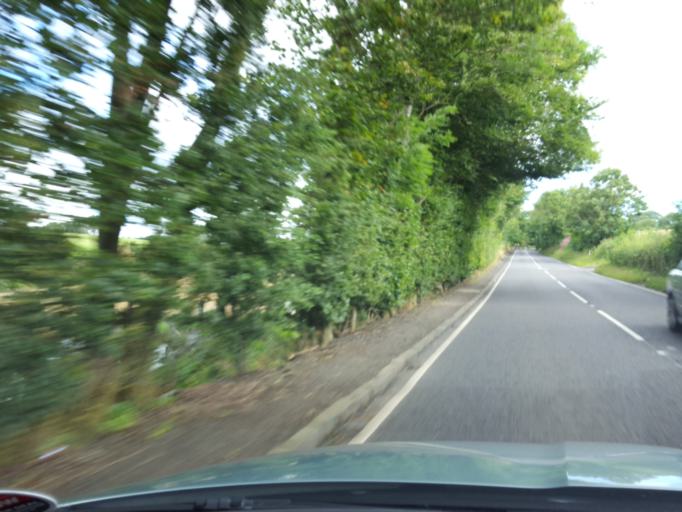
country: GB
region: Scotland
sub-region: West Lothian
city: Linlithgow
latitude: 55.9873
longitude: -3.6140
